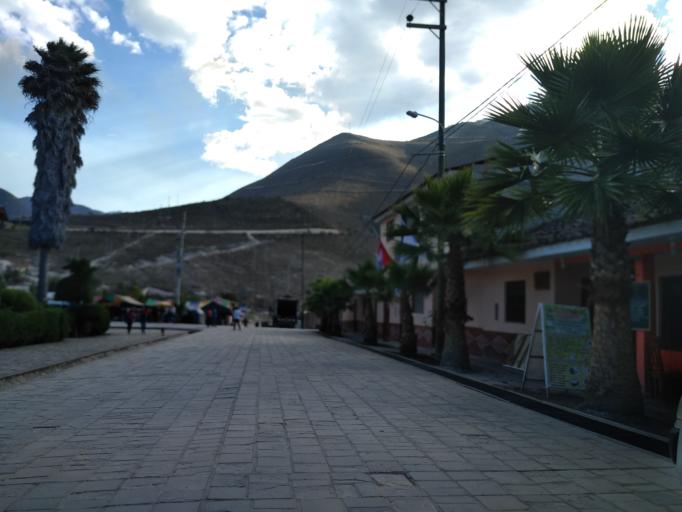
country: PE
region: Amazonas
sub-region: Provincia de Luya
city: Tingo
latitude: -6.3728
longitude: -77.9102
